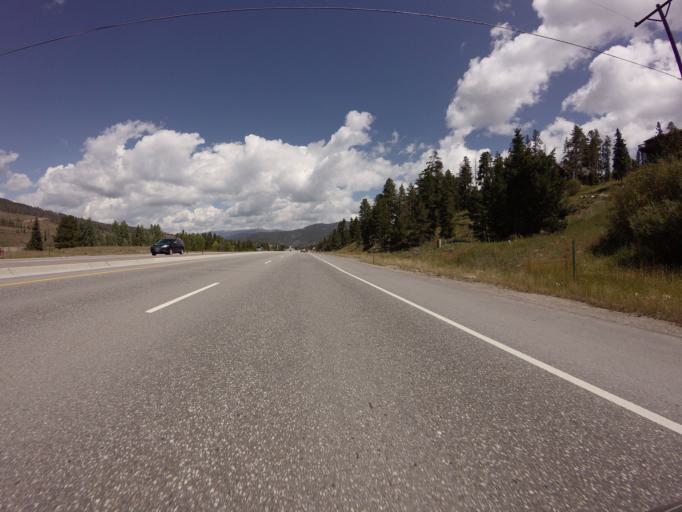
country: US
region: Colorado
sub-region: Summit County
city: Breckenridge
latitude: 39.5214
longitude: -106.0468
